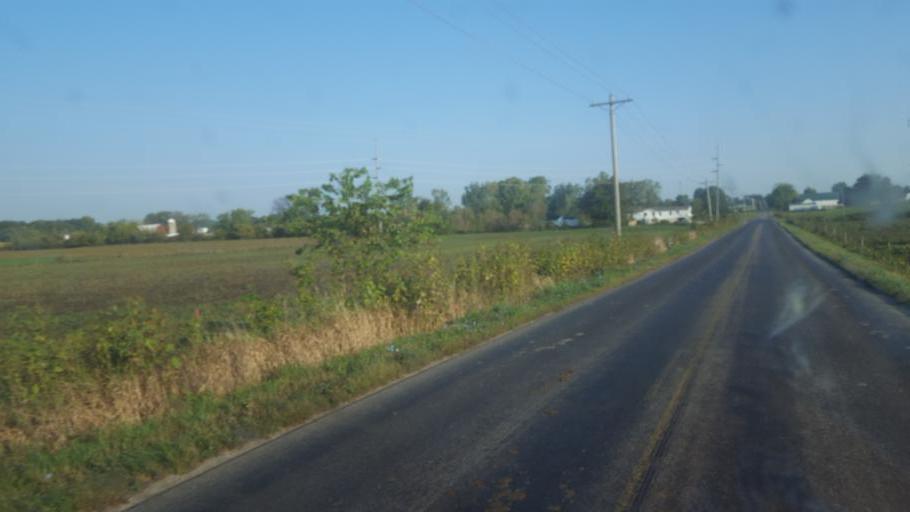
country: US
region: Indiana
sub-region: LaGrange County
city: Lagrange
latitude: 41.6106
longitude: -85.4243
